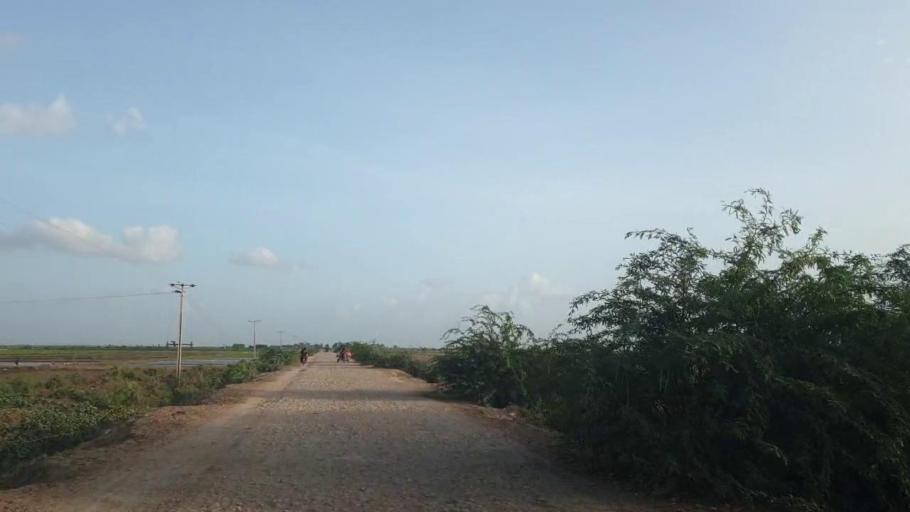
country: PK
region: Sindh
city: Kadhan
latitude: 24.6288
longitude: 69.1158
